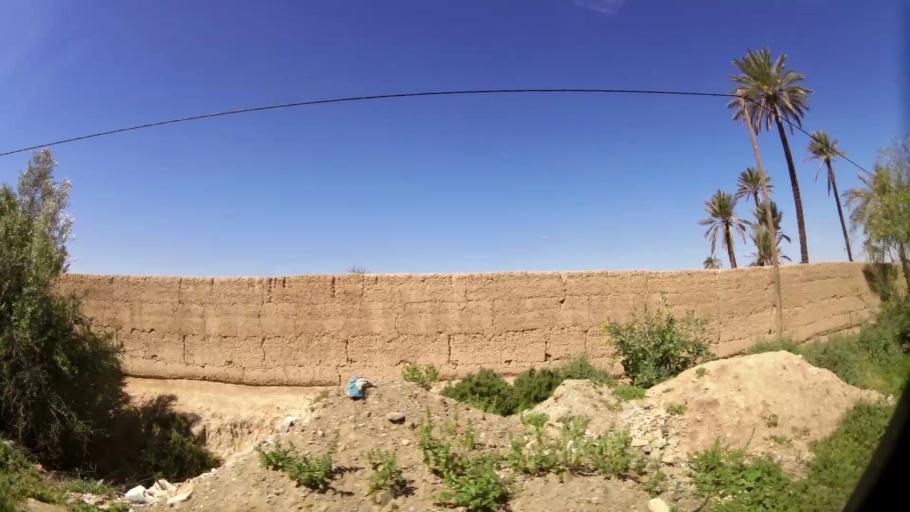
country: MA
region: Marrakech-Tensift-Al Haouz
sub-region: Marrakech
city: Marrakesh
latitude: 31.6714
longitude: -7.9797
